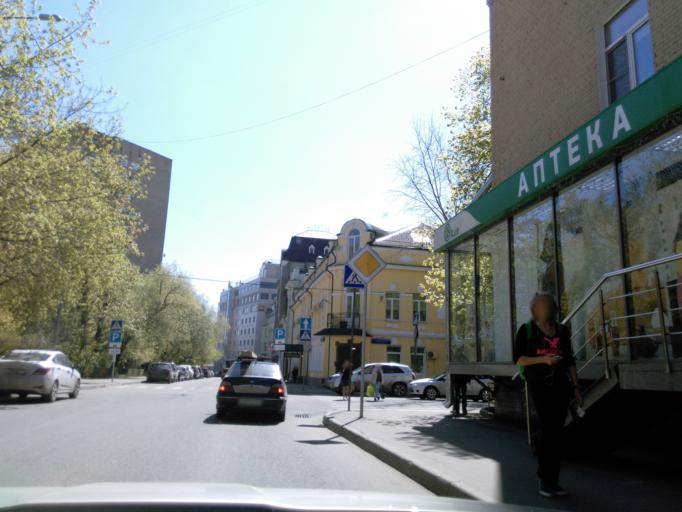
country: RU
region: Moscow
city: Zamoskvorech'ye
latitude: 55.7251
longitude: 37.6328
